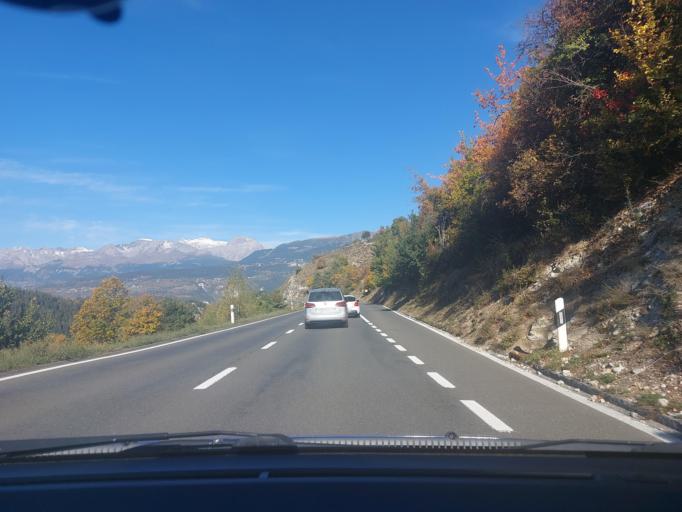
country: CH
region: Valais
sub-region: Sierre District
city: Chippis
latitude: 46.2640
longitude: 7.5588
